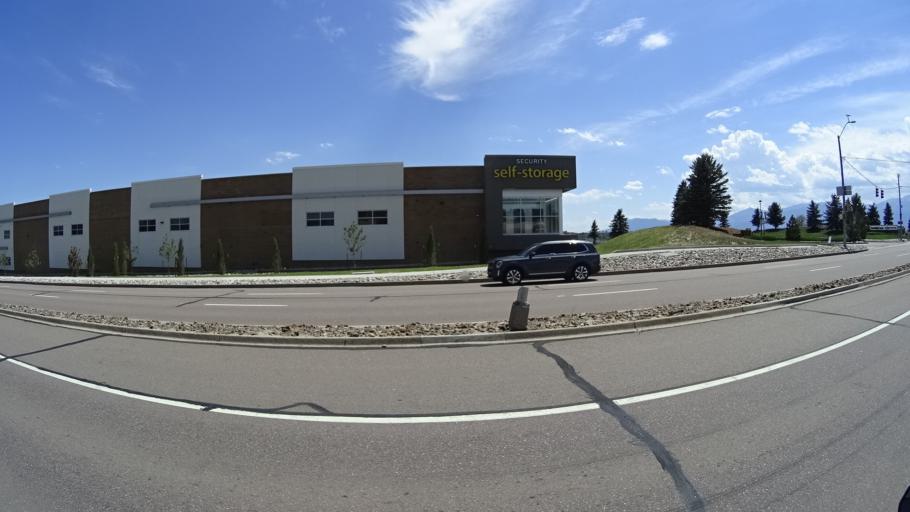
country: US
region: Colorado
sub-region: El Paso County
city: Black Forest
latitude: 38.9403
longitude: -104.7476
